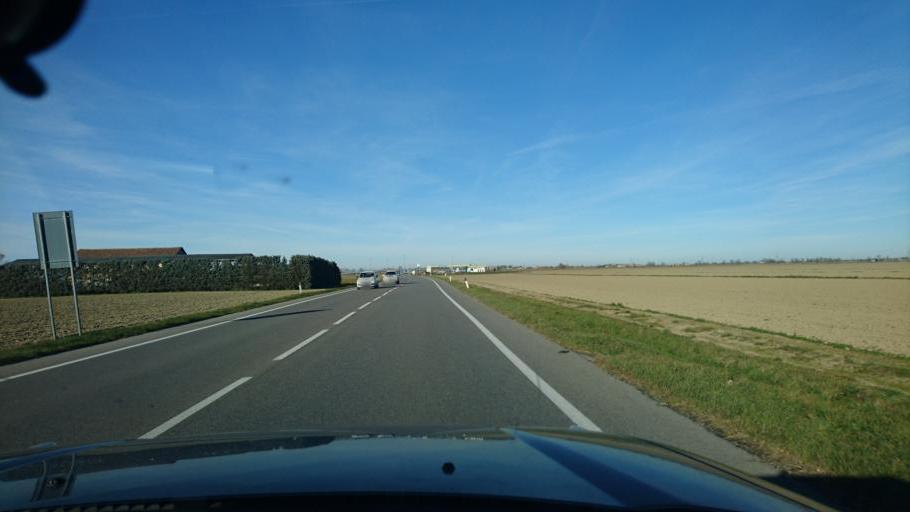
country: IT
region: Veneto
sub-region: Provincia di Rovigo
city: Bottrighe
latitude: 45.0302
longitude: 12.0992
